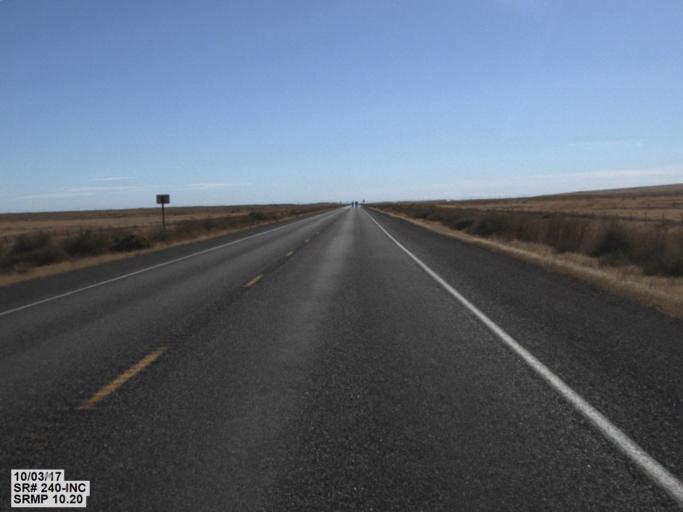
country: US
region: Washington
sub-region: Benton County
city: Benton City
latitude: 46.4840
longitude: -119.5776
